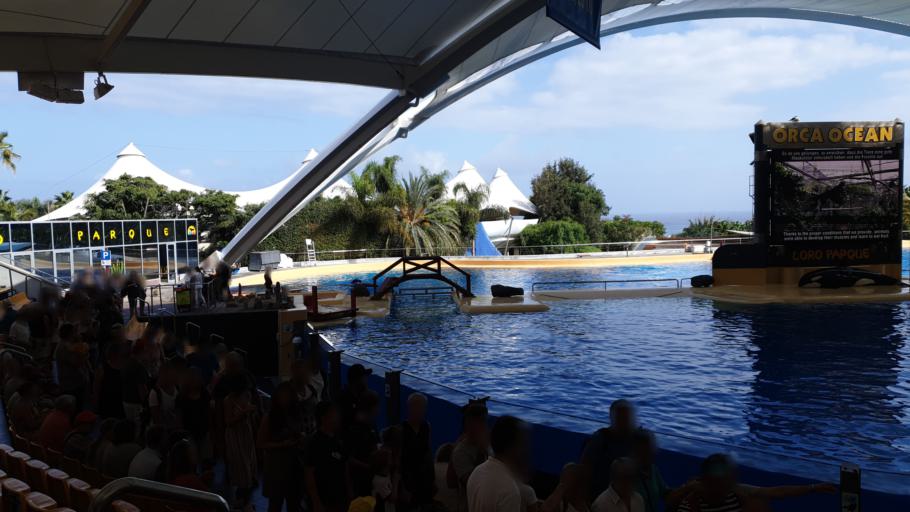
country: ES
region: Canary Islands
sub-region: Provincia de Santa Cruz de Tenerife
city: Puerto de la Cruz
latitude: 28.4078
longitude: -16.5636
